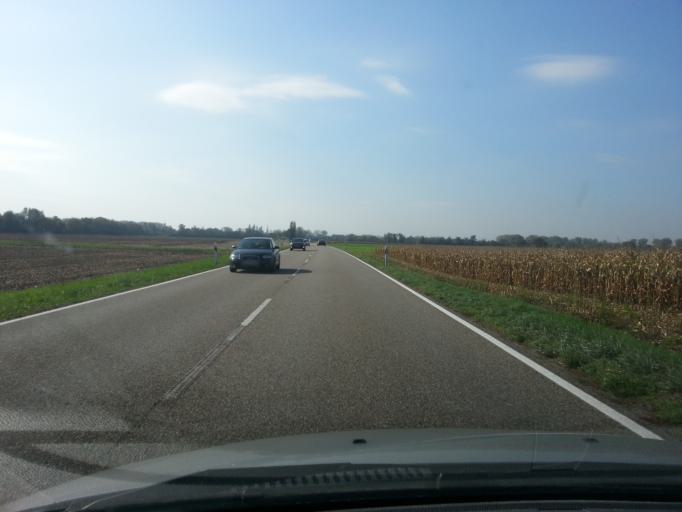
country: DE
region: Baden-Wuerttemberg
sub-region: Karlsruhe Region
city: Altlussheim
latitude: 49.3261
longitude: 8.4809
